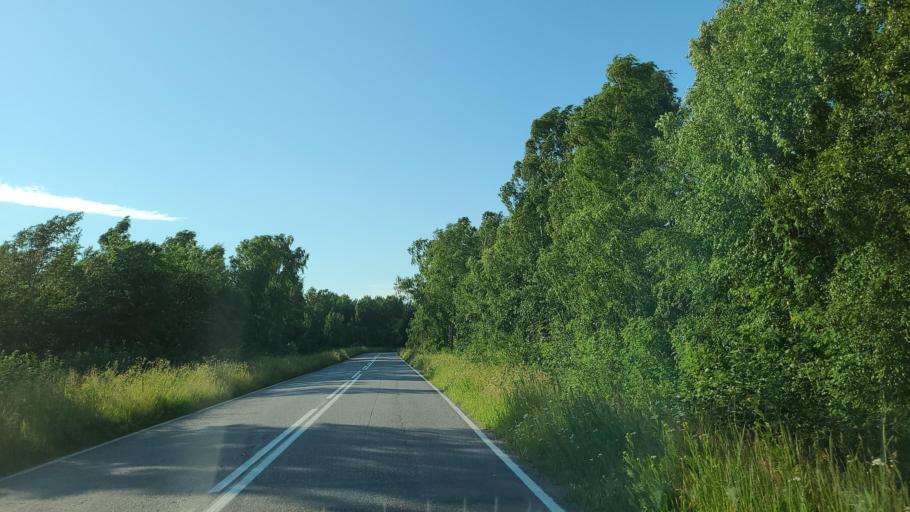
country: FI
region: Ostrobothnia
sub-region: Vaasa
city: Replot
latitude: 63.2841
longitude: 21.3347
